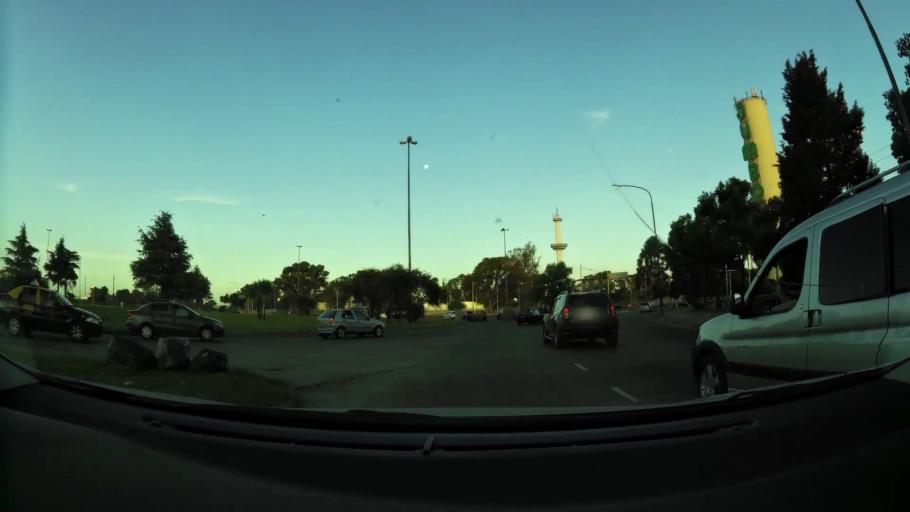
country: AR
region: Buenos Aires F.D.
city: Villa Lugano
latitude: -34.6738
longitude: -58.4593
